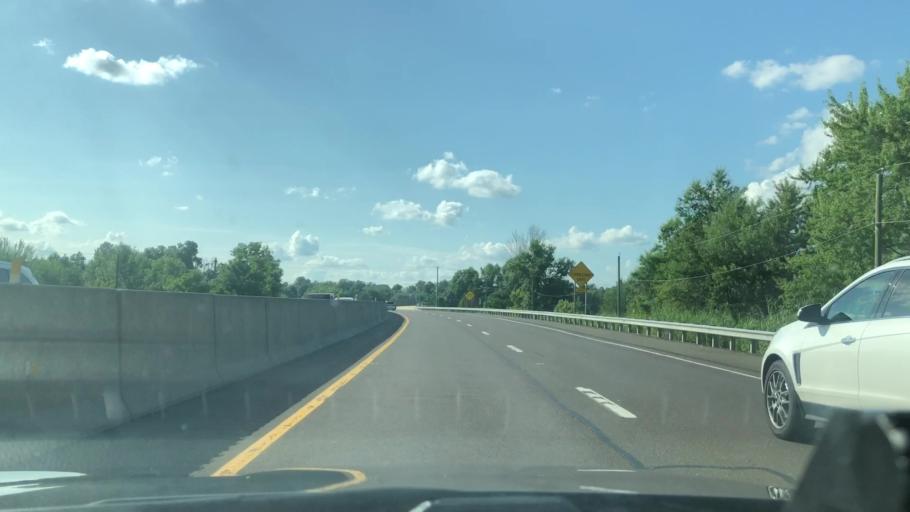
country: US
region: Pennsylvania
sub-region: Montgomery County
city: Spring House
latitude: 40.1890
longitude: -75.2135
